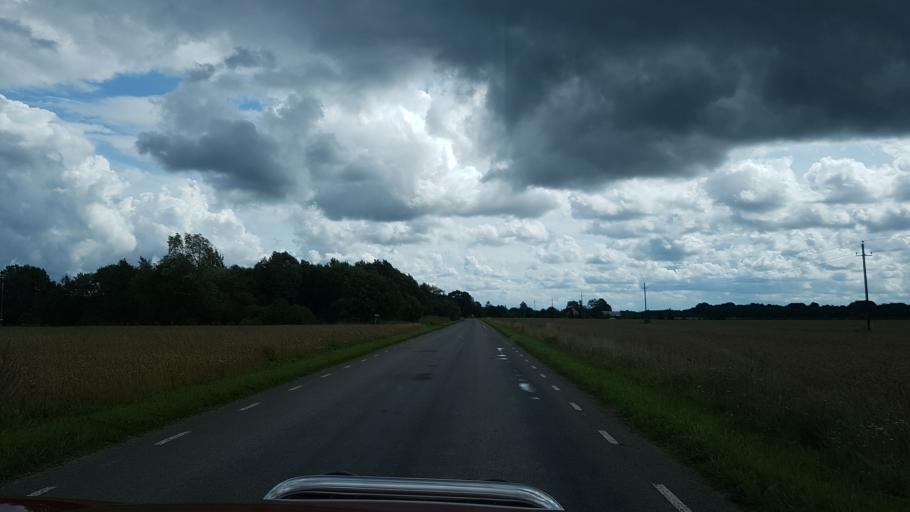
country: EE
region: Laeaene
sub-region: Lihula vald
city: Lihula
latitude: 58.7144
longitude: 23.9998
